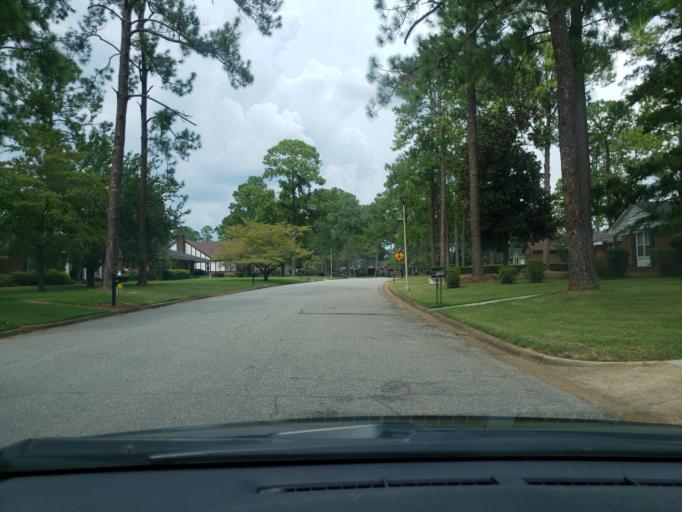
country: US
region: Georgia
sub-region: Dougherty County
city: Albany
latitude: 31.5987
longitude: -84.2064
